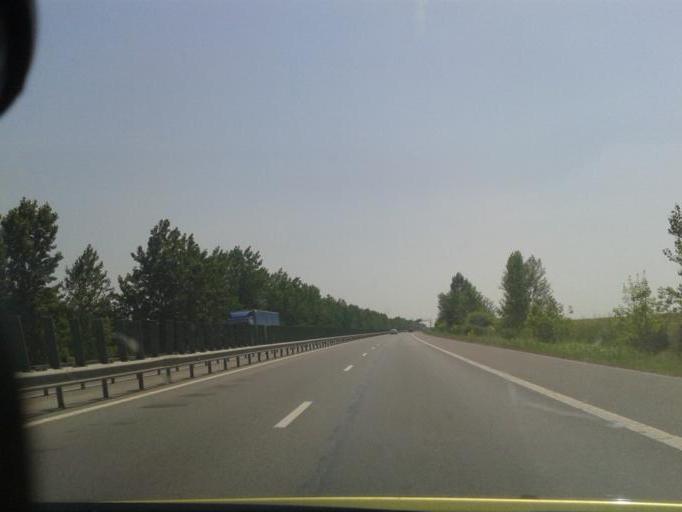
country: RO
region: Calarasi
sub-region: Comuna Fundulea
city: Fundulea
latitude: 44.4483
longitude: 26.5255
